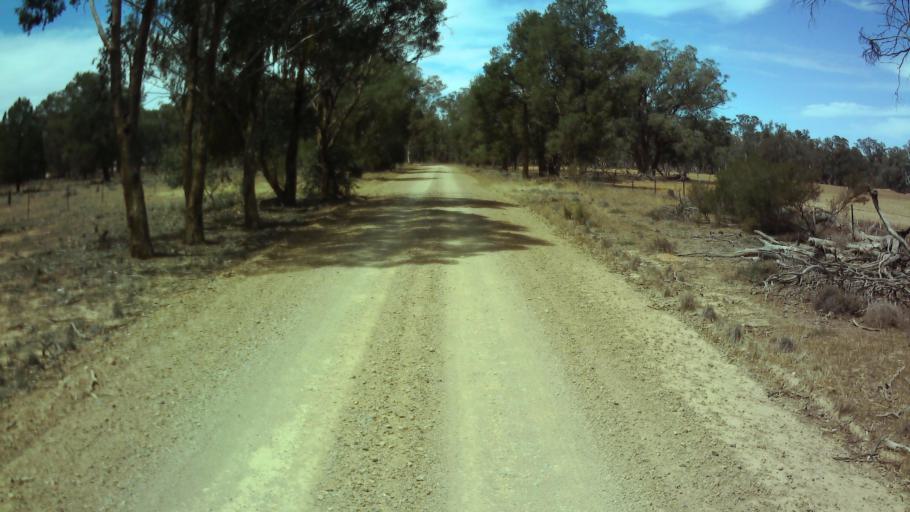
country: AU
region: New South Wales
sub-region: Weddin
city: Grenfell
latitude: -33.8556
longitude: 147.8053
